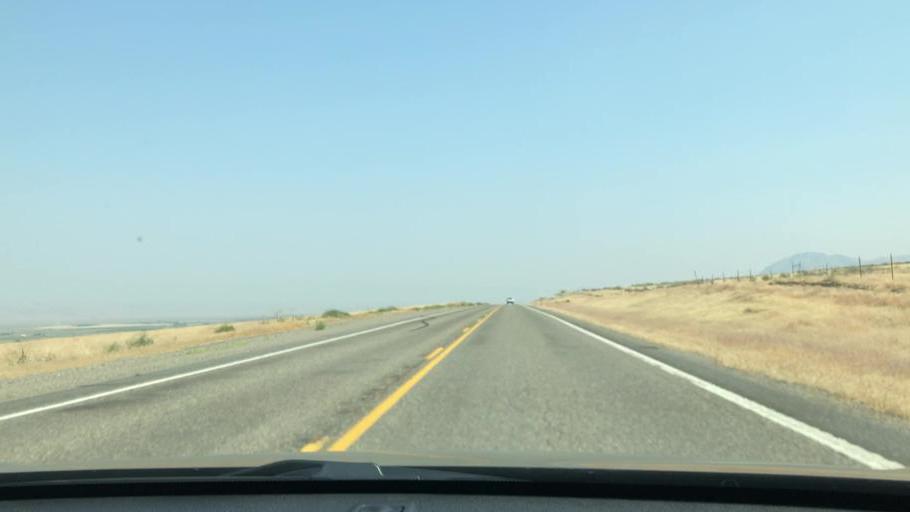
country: US
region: Nevada
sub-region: Humboldt County
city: Winnemucca
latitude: 41.4213
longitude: -117.7895
